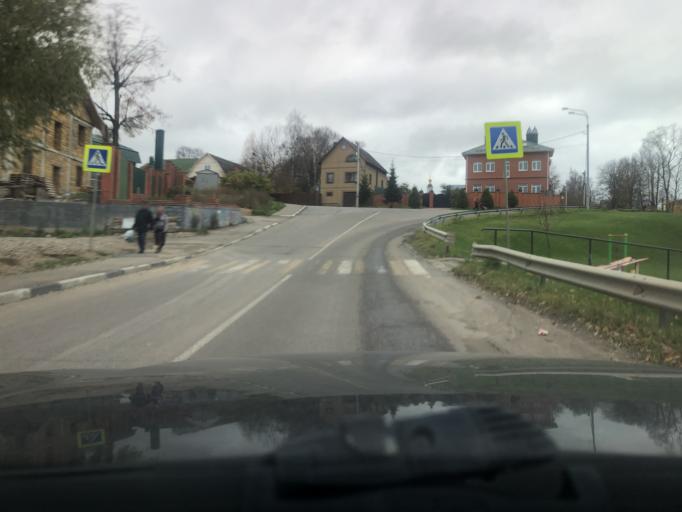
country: RU
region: Moskovskaya
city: Sergiyev Posad
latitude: 56.3032
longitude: 38.1245
